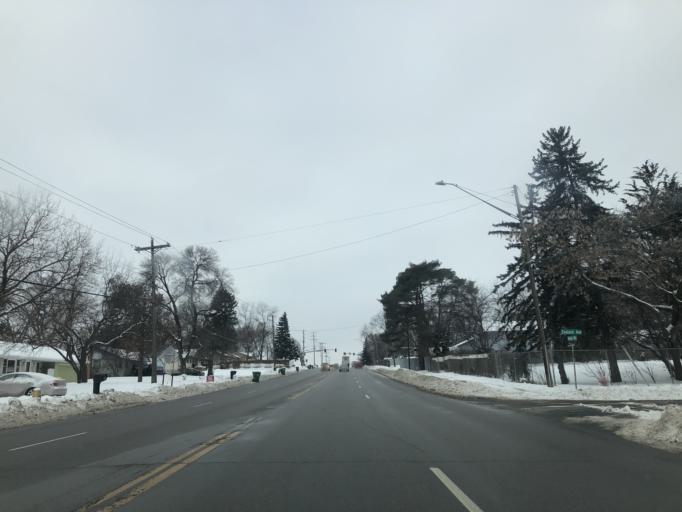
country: US
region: Minnesota
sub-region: Hennepin County
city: Osseo
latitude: 45.0946
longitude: -93.3890
